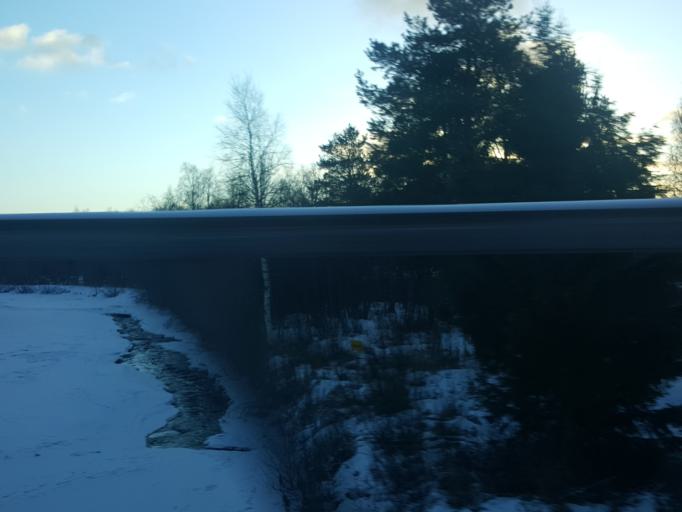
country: SE
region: Jaemtland
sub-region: Harjedalens Kommun
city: Sveg
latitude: 62.4445
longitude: 13.8707
